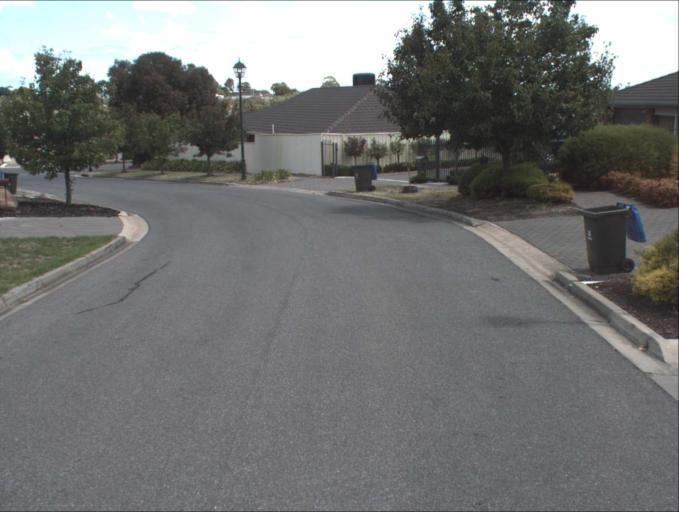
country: AU
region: South Australia
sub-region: Port Adelaide Enfield
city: Gilles Plains
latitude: -34.8443
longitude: 138.6473
